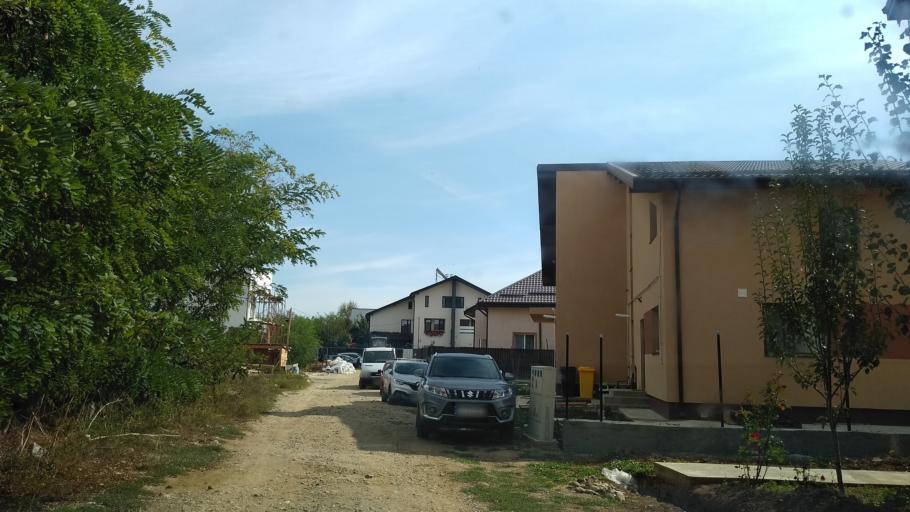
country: RO
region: Ilfov
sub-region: Comuna Chitila
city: Chitila
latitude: 44.5149
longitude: 25.9879
